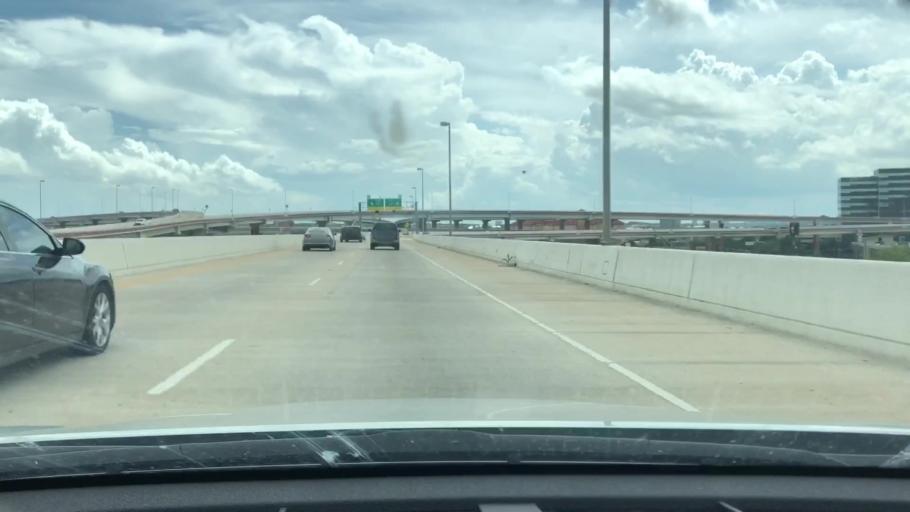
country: US
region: Texas
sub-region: Bexar County
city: Castle Hills
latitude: 29.5242
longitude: -98.4821
